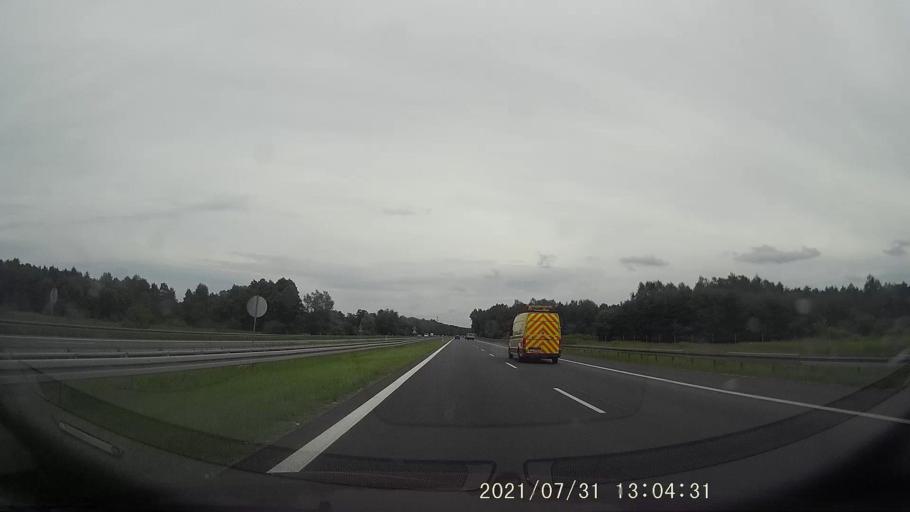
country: PL
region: Lesser Poland Voivodeship
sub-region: Powiat oswiecimski
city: Chelmek
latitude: 50.1498
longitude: 19.2711
